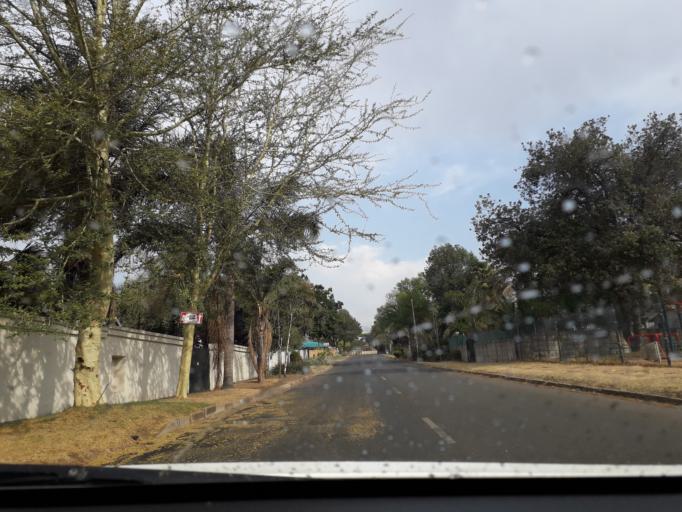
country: ZA
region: Gauteng
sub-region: City of Johannesburg Metropolitan Municipality
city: Modderfontein
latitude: -26.0925
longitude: 28.2463
